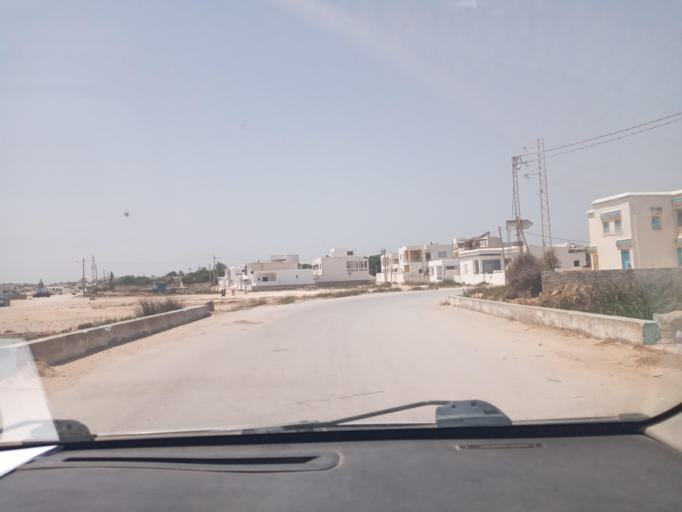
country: TN
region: Nabul
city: El Haouaria
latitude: 37.0410
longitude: 11.0620
